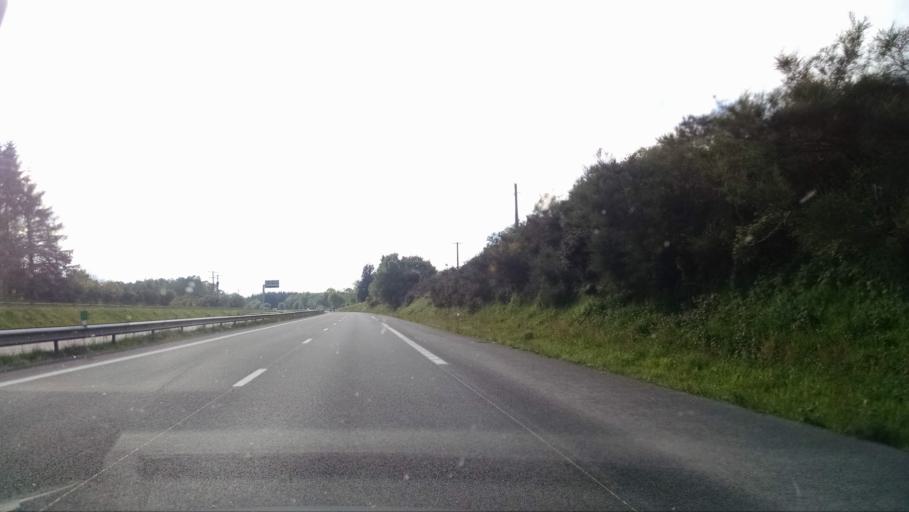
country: FR
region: Brittany
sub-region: Departement du Finistere
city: Guerlesquin
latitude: 48.5658
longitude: -3.5462
